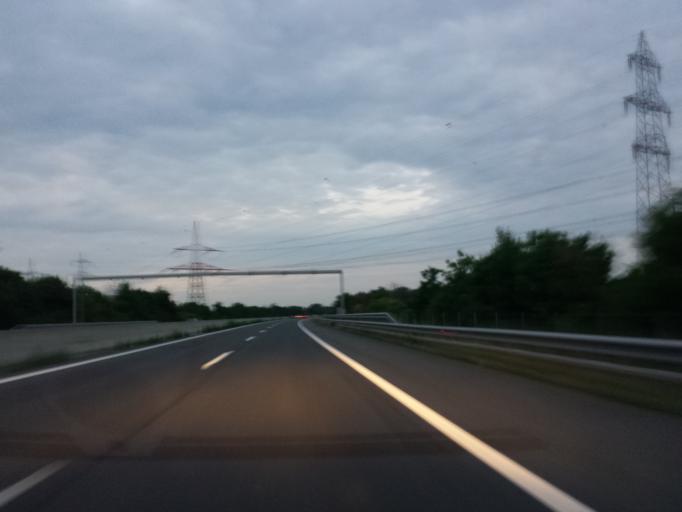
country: AT
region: Lower Austria
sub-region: Politischer Bezirk Baden
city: Trumau
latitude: 47.9781
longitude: 16.3728
